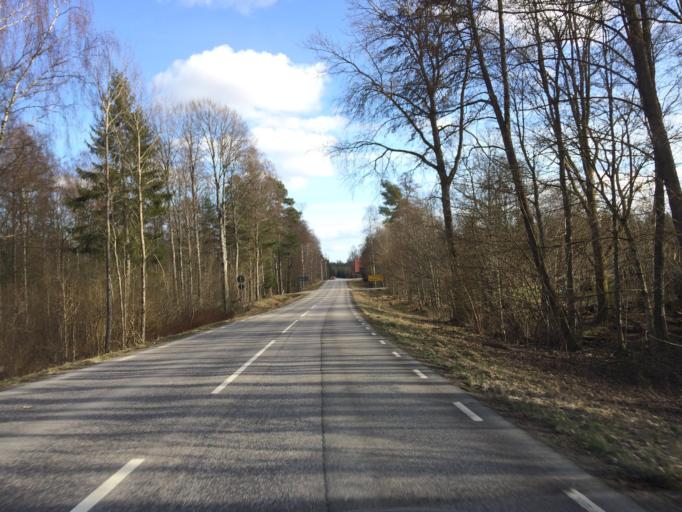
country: SE
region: Kronoberg
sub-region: Almhults Kommun
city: AElmhult
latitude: 56.5733
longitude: 14.1147
